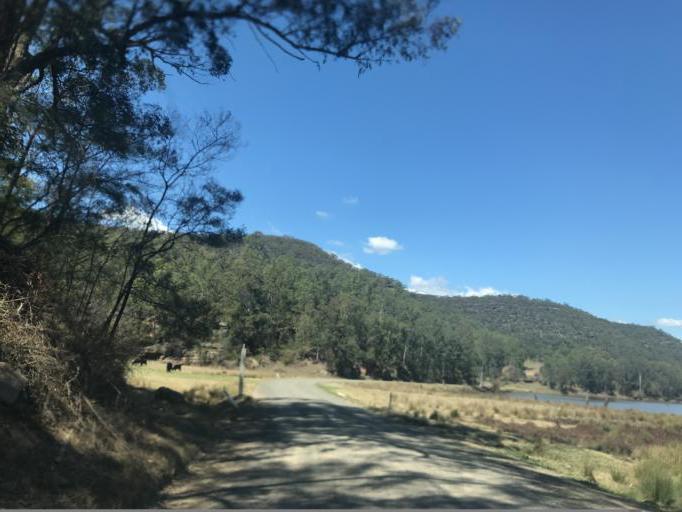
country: AU
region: New South Wales
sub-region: Hornsby Shire
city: Glenorie
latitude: -33.2484
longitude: 150.9761
